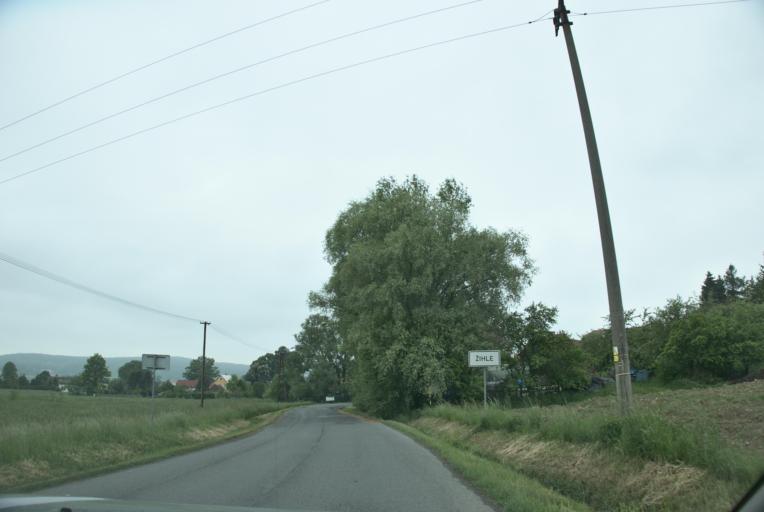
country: CZ
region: Plzensky
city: Zihle
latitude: 50.0431
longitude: 13.3845
